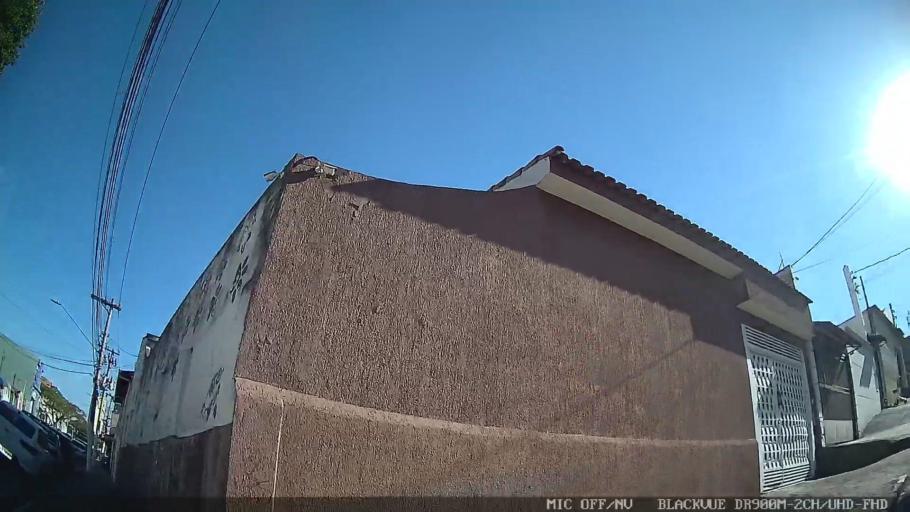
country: BR
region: Sao Paulo
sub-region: Guarulhos
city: Guarulhos
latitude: -23.5336
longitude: -46.5215
